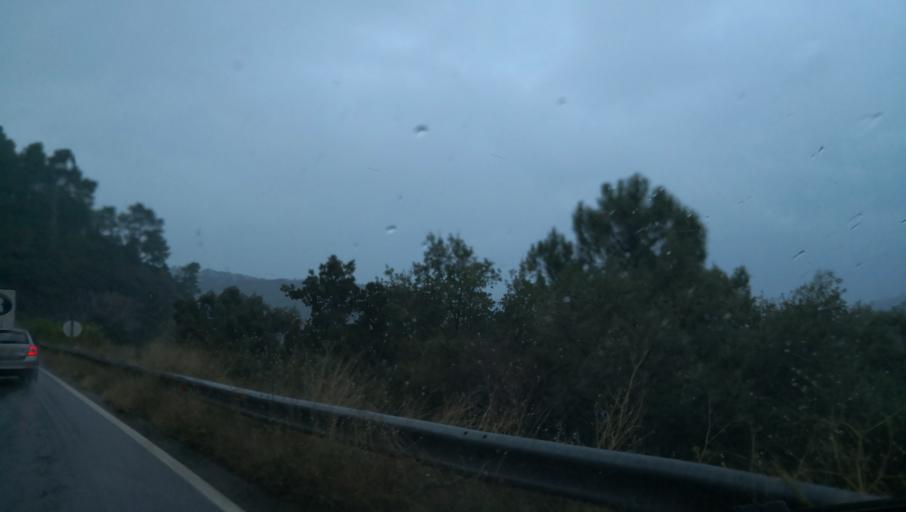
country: PT
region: Vila Real
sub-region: Santa Marta de Penaguiao
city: Santa Marta de Penaguiao
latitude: 41.2133
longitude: -7.7283
